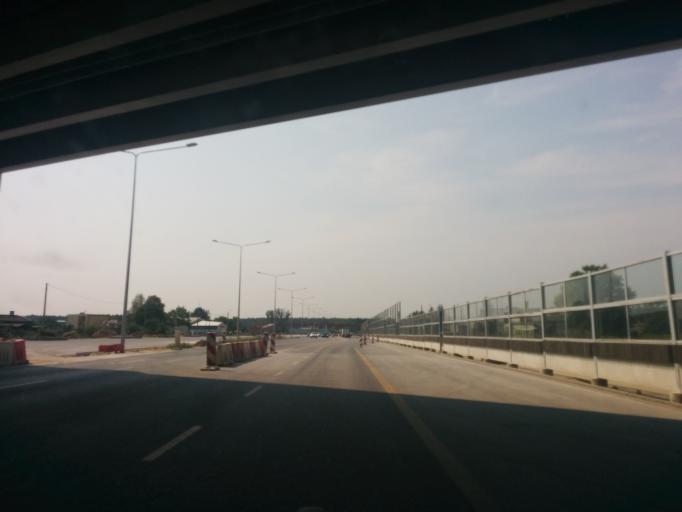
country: PL
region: Masovian Voivodeship
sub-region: Powiat pruszkowski
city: Michalowice
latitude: 52.1198
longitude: 20.8689
